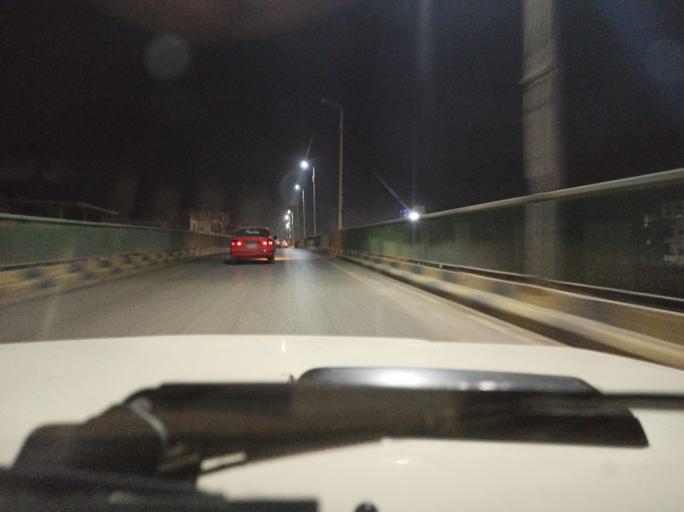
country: EG
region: Muhafazat Bani Suwayf
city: Bani Suwayf
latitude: 29.0760
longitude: 31.0914
